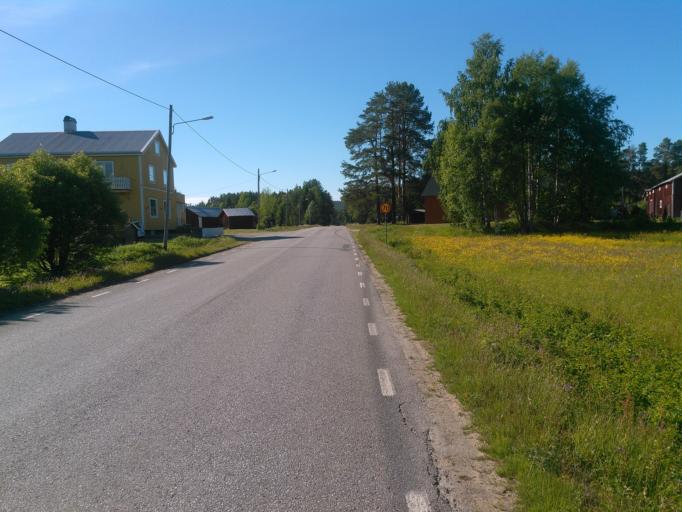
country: SE
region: Vaesterbotten
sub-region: Umea Kommun
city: Roback
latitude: 63.8291
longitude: 20.1153
